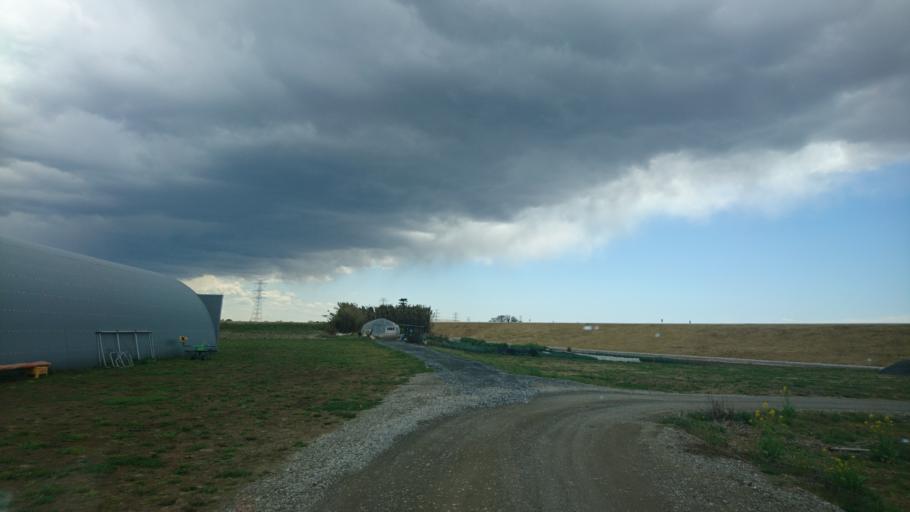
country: JP
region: Ibaraki
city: Yuki
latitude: 36.2727
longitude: 139.9073
